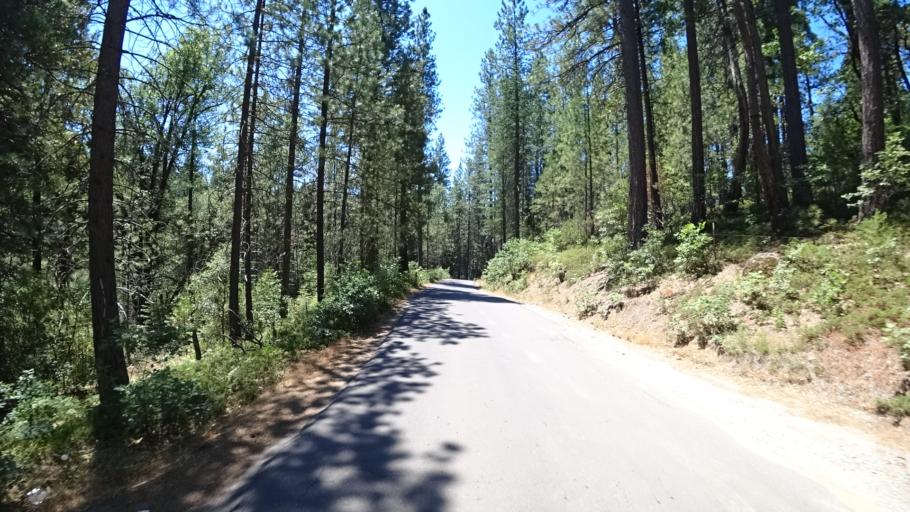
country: US
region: California
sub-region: Calaveras County
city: Arnold
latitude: 38.2156
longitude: -120.3600
